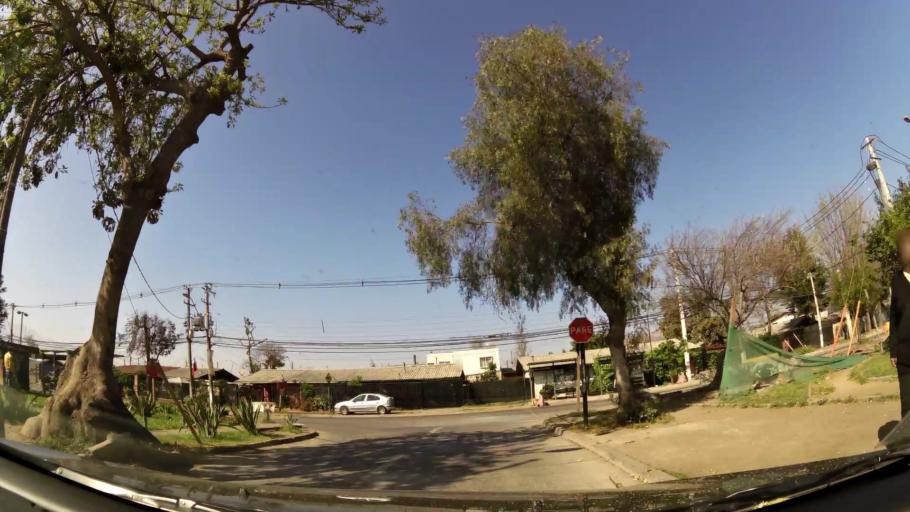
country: CL
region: Santiago Metropolitan
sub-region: Provincia de Chacabuco
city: Chicureo Abajo
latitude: -33.3596
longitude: -70.6895
